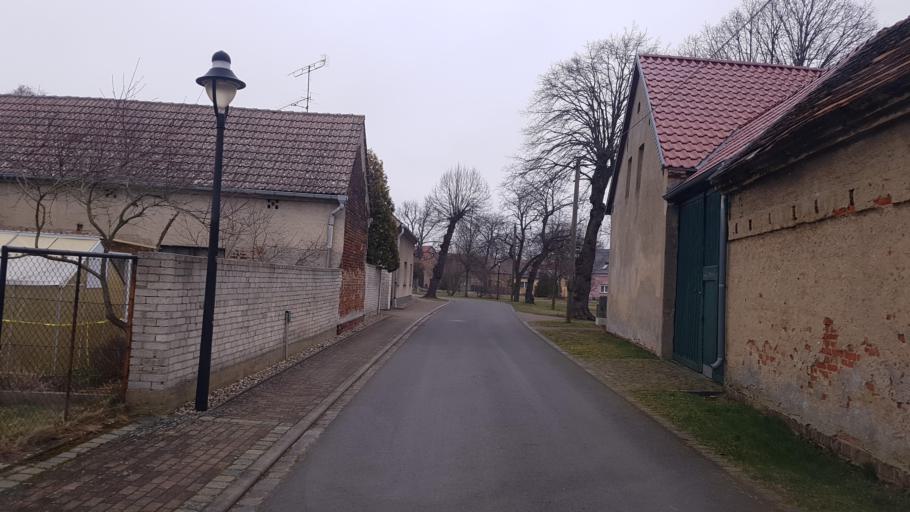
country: DE
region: Brandenburg
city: Herzberg
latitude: 51.6839
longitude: 13.2741
